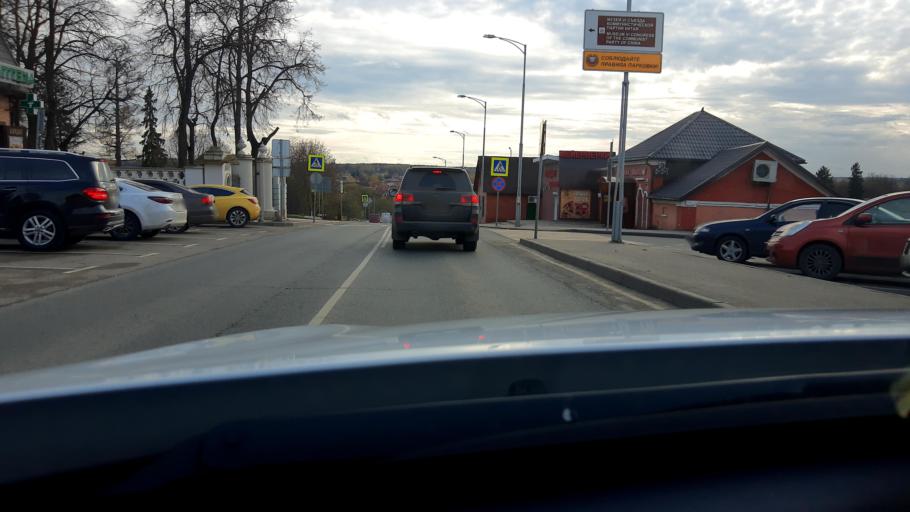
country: RU
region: Moskovskaya
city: Kokoshkino
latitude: 55.5365
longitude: 37.1529
